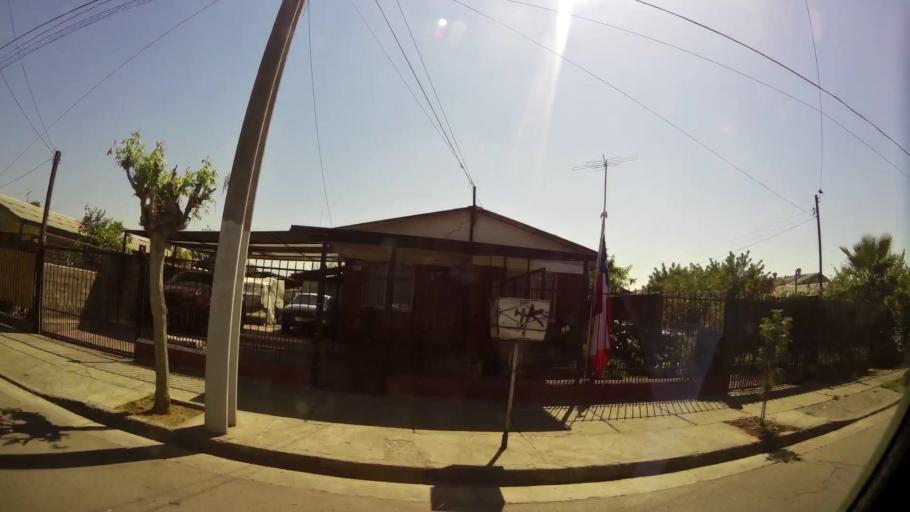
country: CL
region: Santiago Metropolitan
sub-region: Provincia de Talagante
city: Penaflor
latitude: -33.5688
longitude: -70.8119
